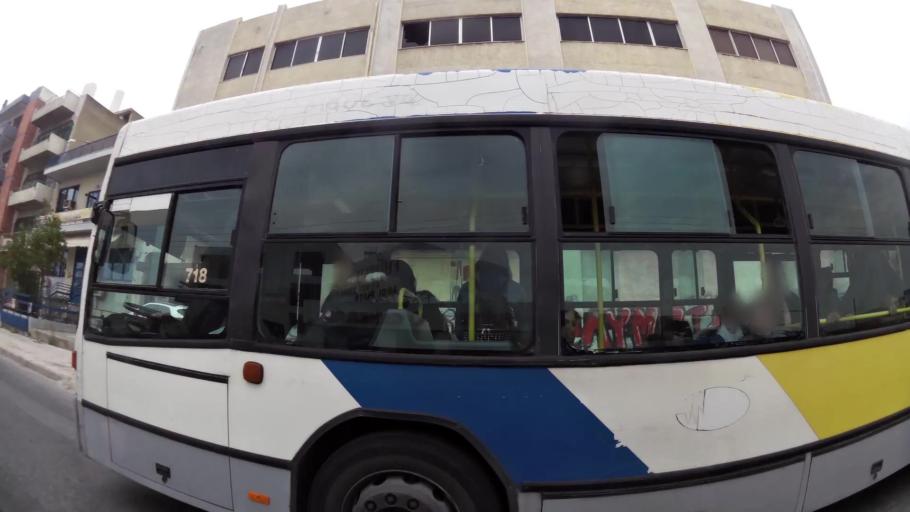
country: GR
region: Attica
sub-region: Nomos Piraios
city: Agios Ioannis Rentis
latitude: 37.9719
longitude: 23.6645
